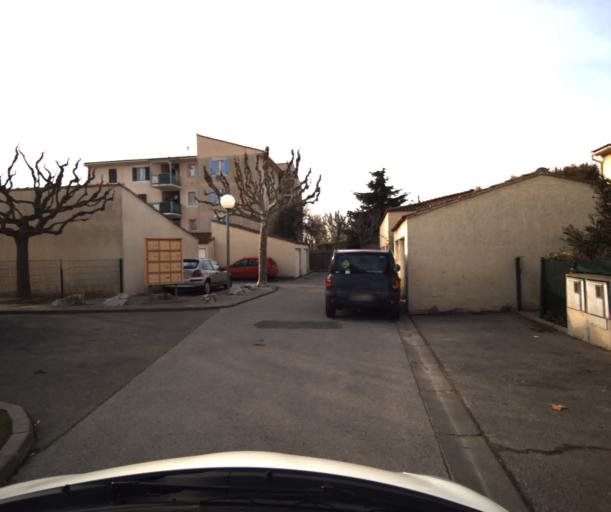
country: FR
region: Provence-Alpes-Cote d'Azur
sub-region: Departement du Vaucluse
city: Pertuis
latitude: 43.6911
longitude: 5.4920
